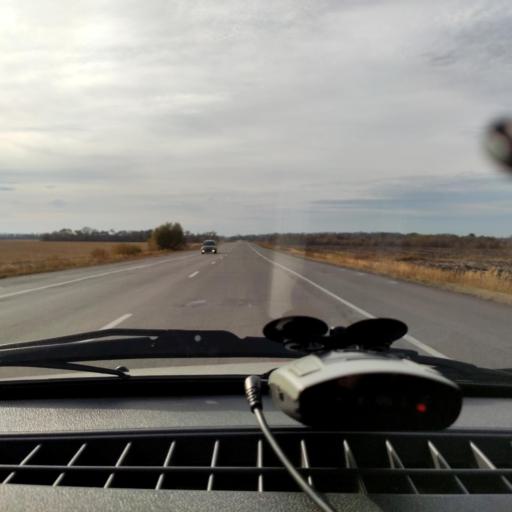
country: RU
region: Voronezj
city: Devitsa
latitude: 51.5845
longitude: 38.9763
